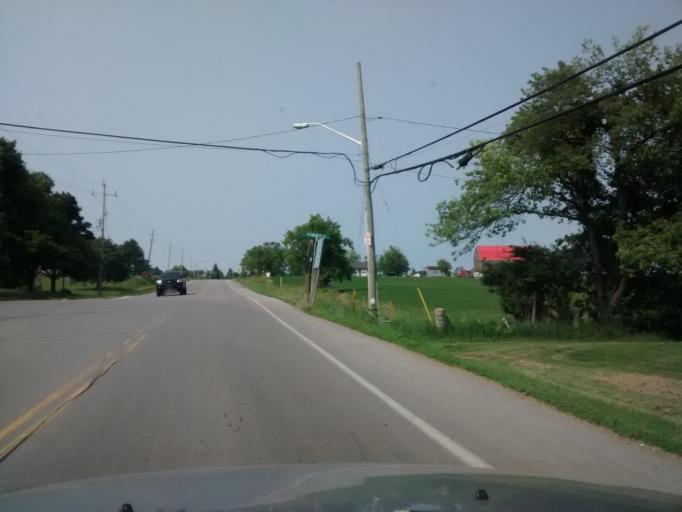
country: CA
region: Ontario
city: Ancaster
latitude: 43.0835
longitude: -79.9205
